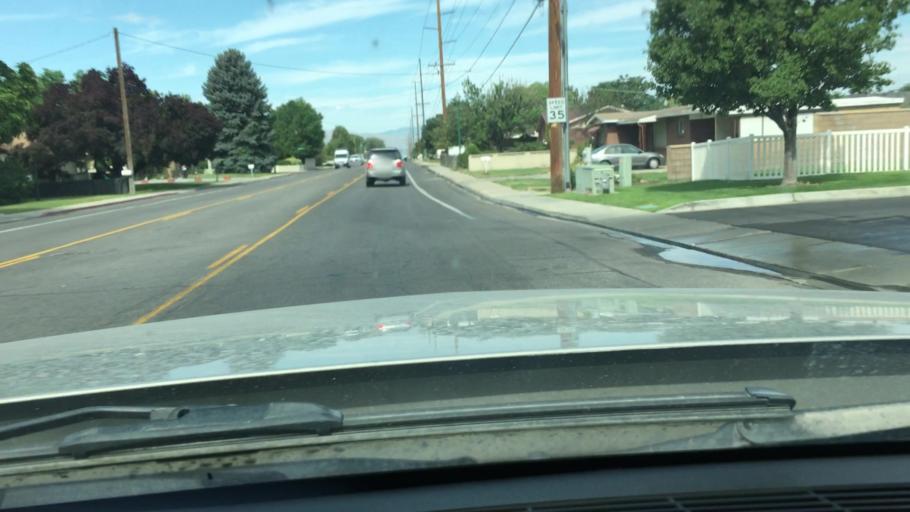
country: US
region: Utah
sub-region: Utah County
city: Lindon
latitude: 40.3265
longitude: -111.7103
